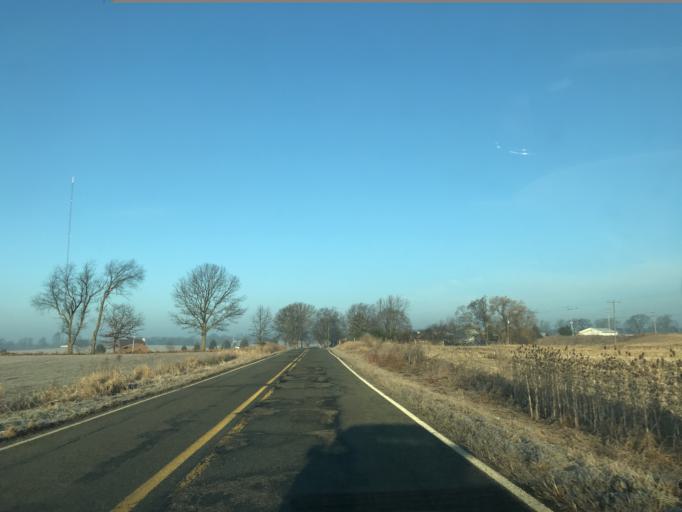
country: US
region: Michigan
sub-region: Ingham County
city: Leslie
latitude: 42.4179
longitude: -84.5104
